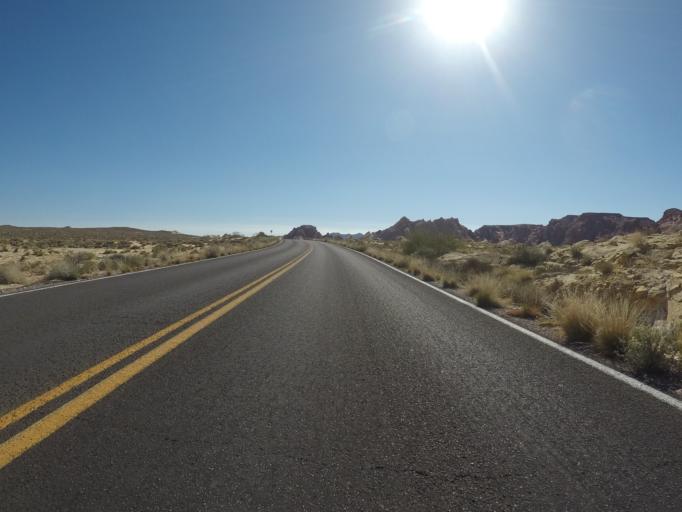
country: US
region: Nevada
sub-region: Clark County
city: Moapa Valley
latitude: 36.4639
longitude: -114.5223
